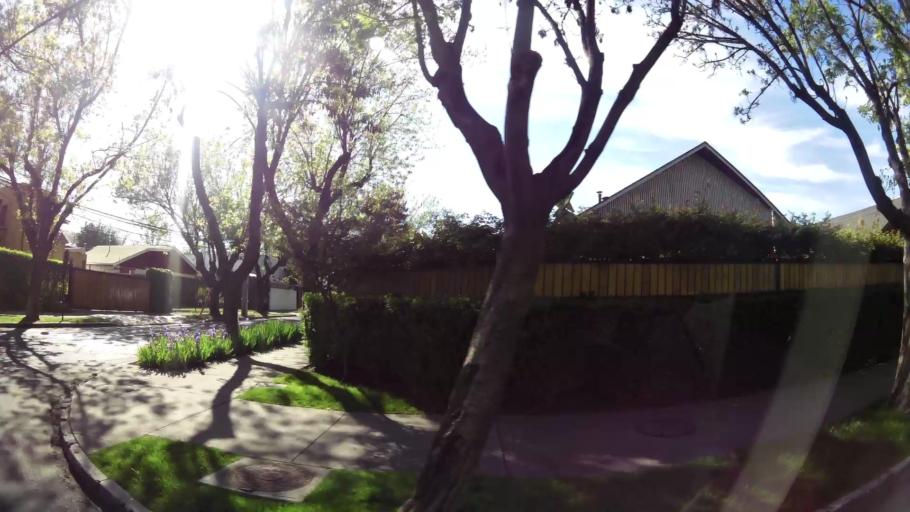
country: CL
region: Santiago Metropolitan
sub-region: Provincia de Santiago
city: Villa Presidente Frei, Nunoa, Santiago, Chile
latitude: -33.4343
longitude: -70.5604
